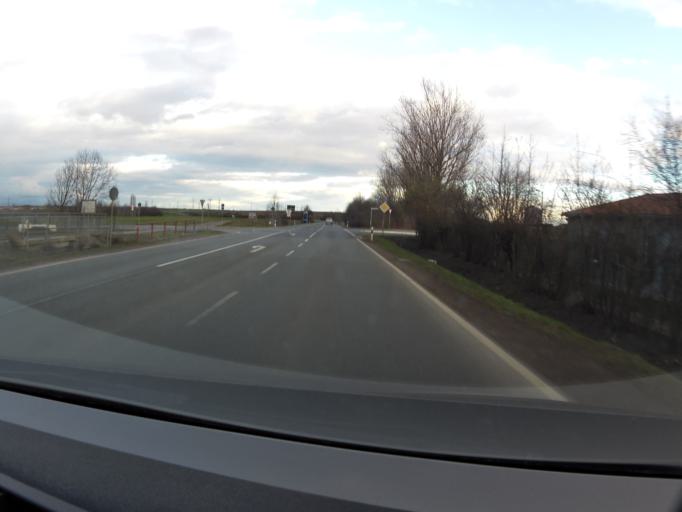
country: DE
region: Thuringia
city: Arnstadt
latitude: 50.8505
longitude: 10.9633
